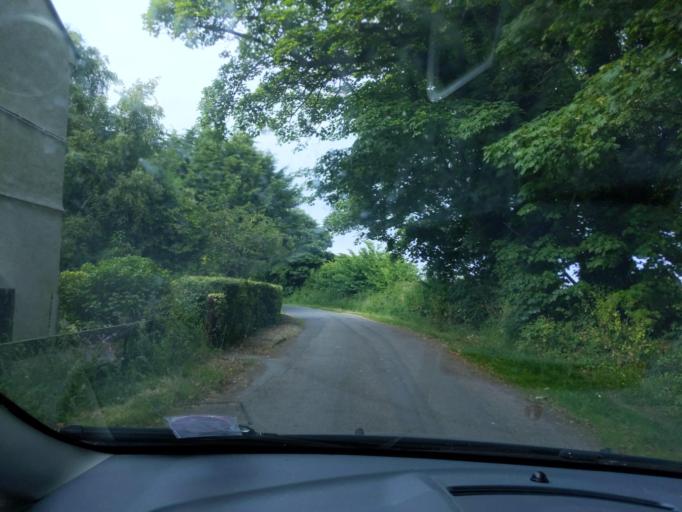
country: IM
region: Ramsey
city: Ramsey
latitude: 54.3563
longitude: -4.4460
